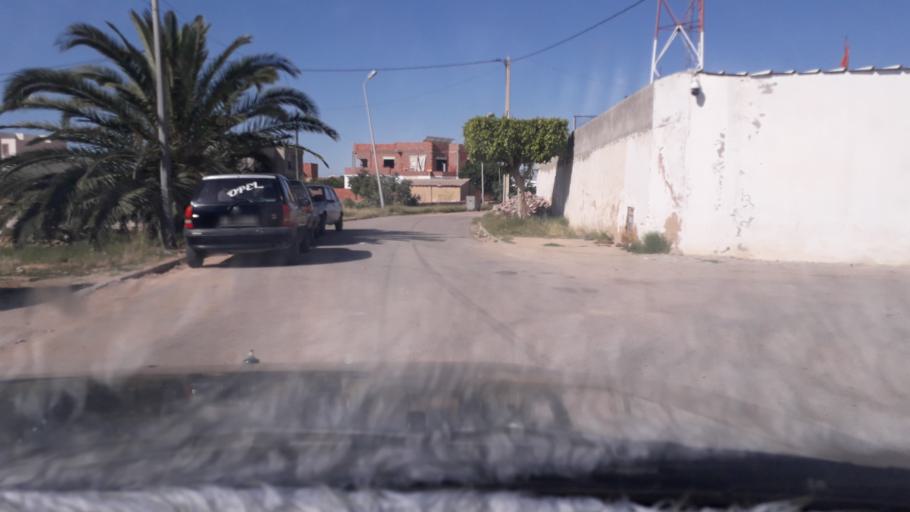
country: TN
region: Safaqis
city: Al Qarmadah
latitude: 34.8236
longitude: 10.7504
